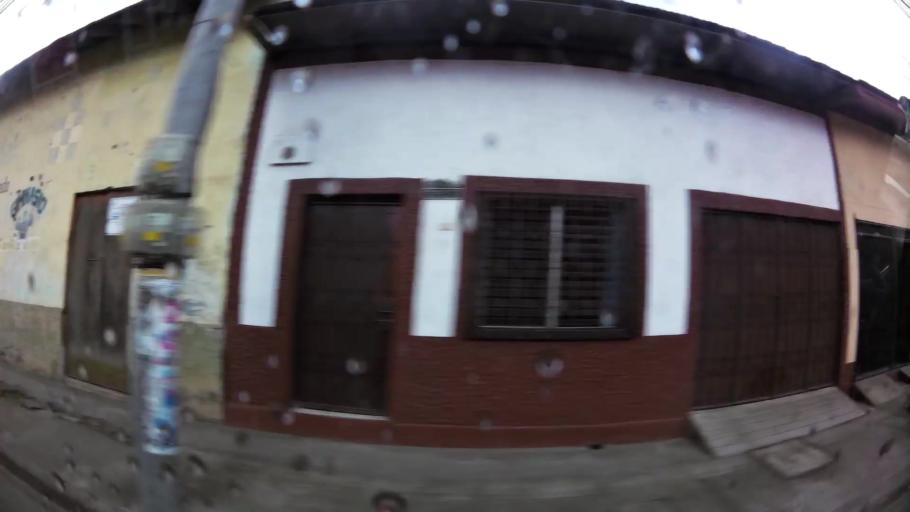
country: NI
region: Jinotega
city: Jinotega
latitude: 13.0963
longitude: -86.0026
